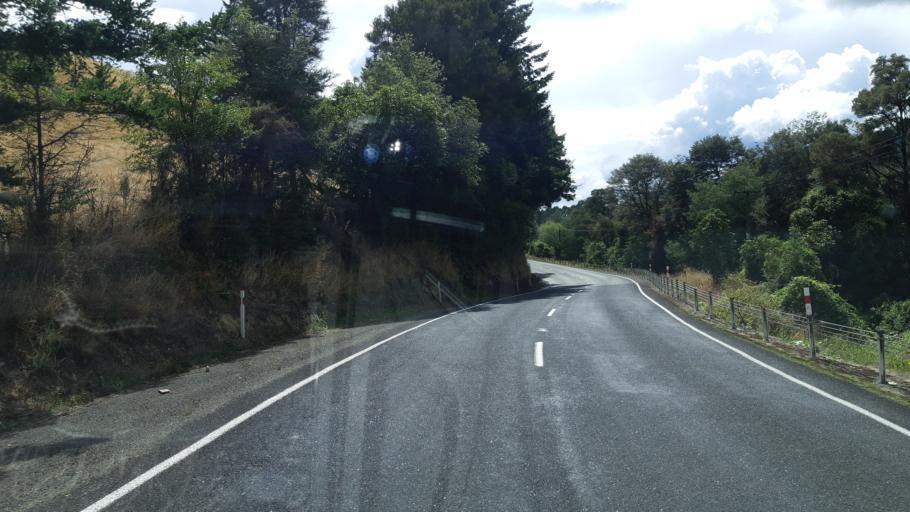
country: NZ
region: Tasman
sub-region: Tasman District
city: Wakefield
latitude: -41.4999
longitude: 172.7950
